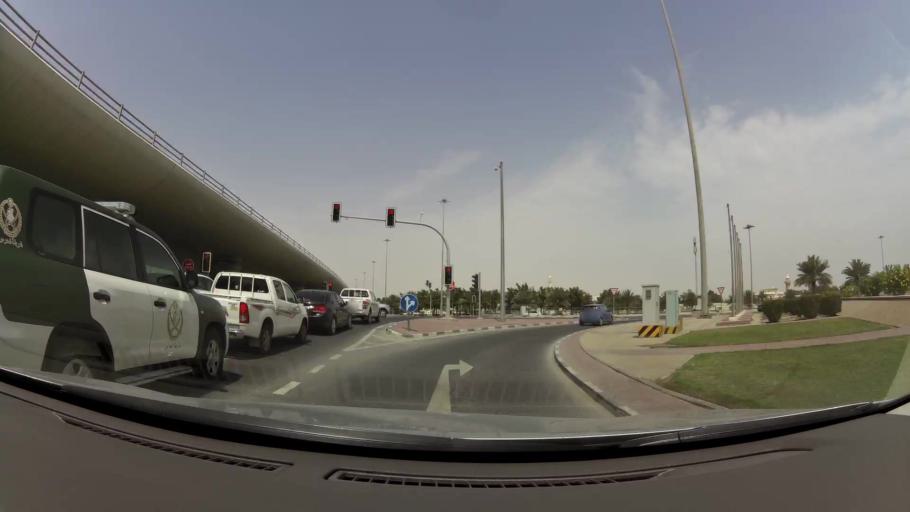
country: QA
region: Baladiyat ar Rayyan
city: Ar Rayyan
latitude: 25.3201
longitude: 51.4704
